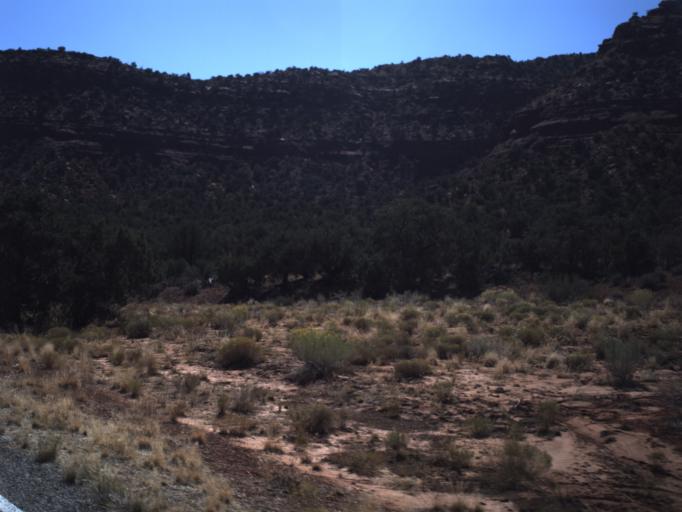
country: US
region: Utah
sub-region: San Juan County
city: Blanding
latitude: 37.6585
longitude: -110.1824
